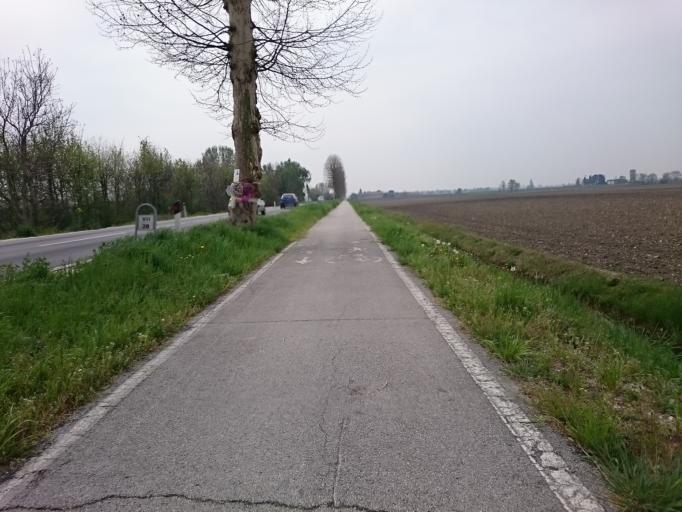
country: IT
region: Veneto
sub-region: Provincia di Padova
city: Bagnoli di Sopra
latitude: 45.1719
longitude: 11.8793
